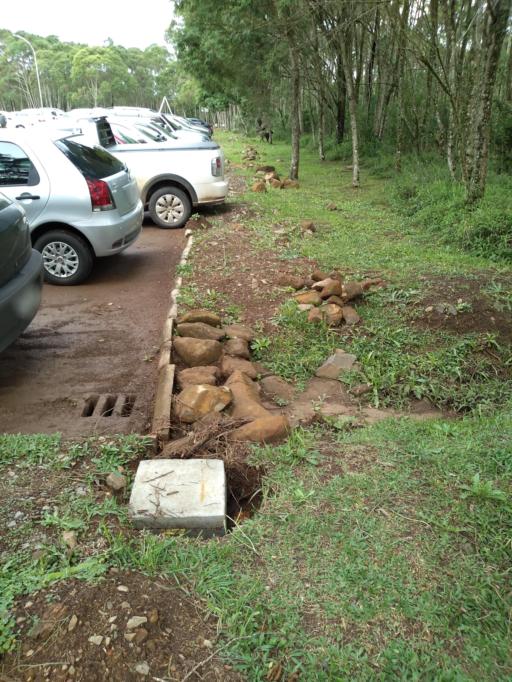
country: BR
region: Santa Catarina
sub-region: Curitibanos
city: Curitibanos
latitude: -27.2851
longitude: -50.5348
